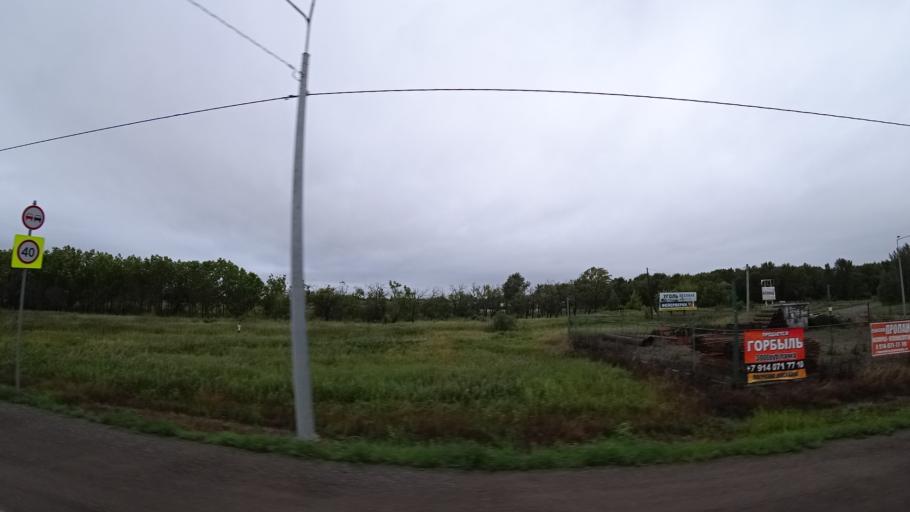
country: RU
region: Primorskiy
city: Chernigovka
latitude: 44.3281
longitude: 132.5729
